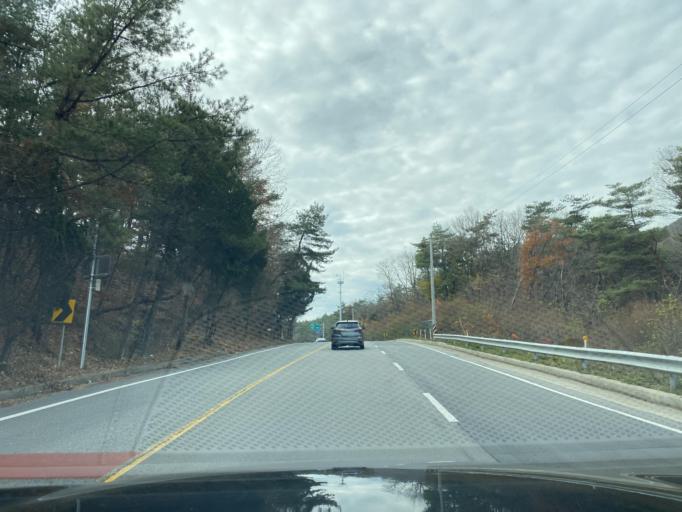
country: KR
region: Chungcheongnam-do
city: Hongsung
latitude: 36.6677
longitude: 126.6379
